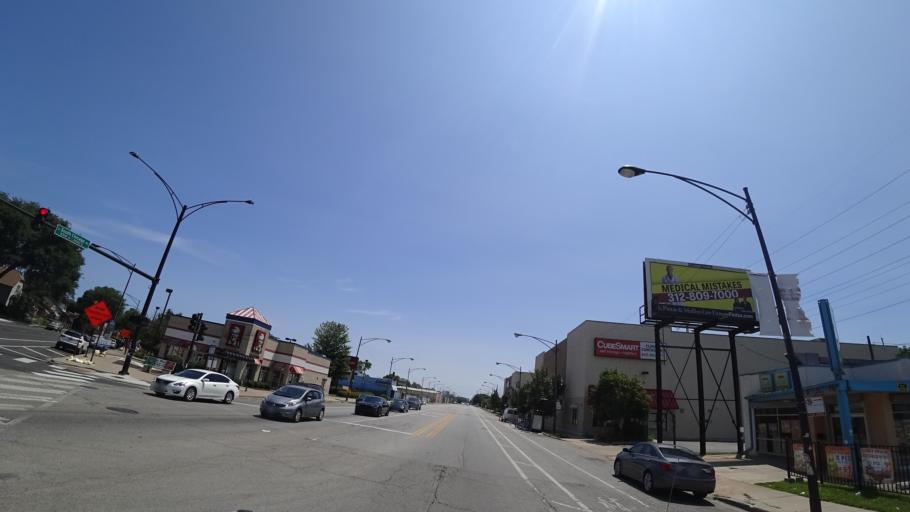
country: US
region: Indiana
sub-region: Lake County
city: Whiting
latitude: 41.7443
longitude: -87.5756
